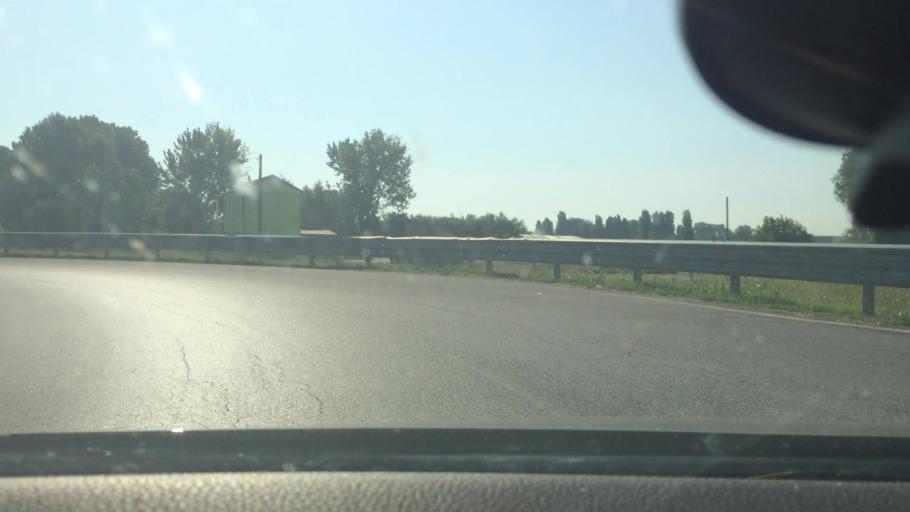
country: IT
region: Emilia-Romagna
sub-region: Provincia di Ferrara
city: Lagosanto
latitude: 44.7466
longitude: 12.1362
